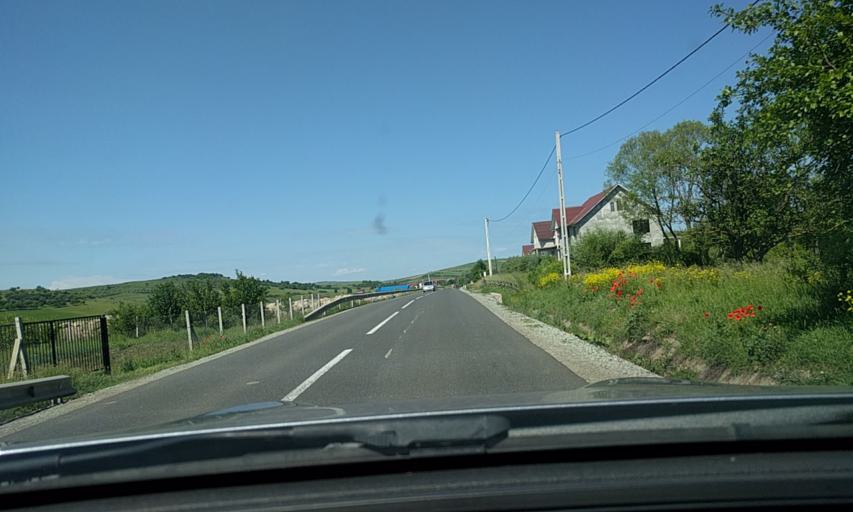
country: RO
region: Bistrita-Nasaud
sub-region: Comuna Dumitra
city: Dumitra
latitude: 47.2319
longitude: 24.4487
